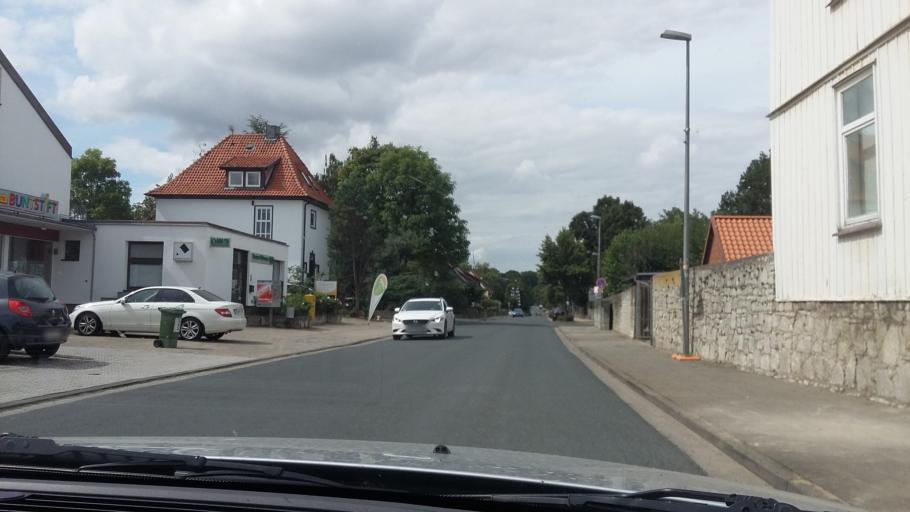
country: DE
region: Lower Saxony
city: Harsum
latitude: 52.2060
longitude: 9.9637
